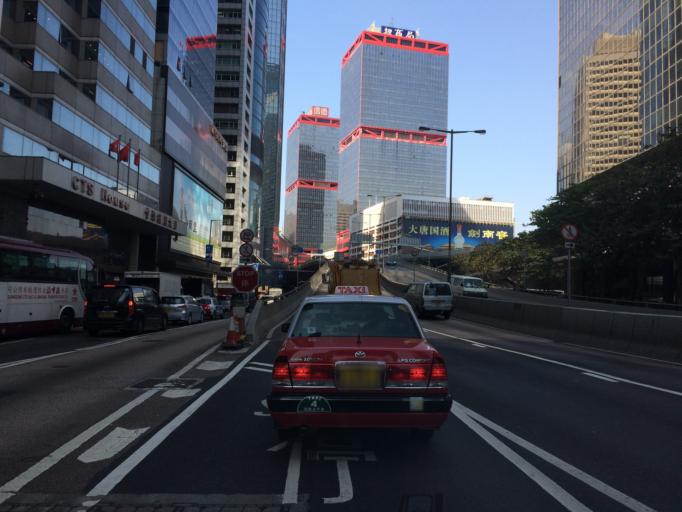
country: HK
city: Hong Kong
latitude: 22.2860
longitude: 114.1553
